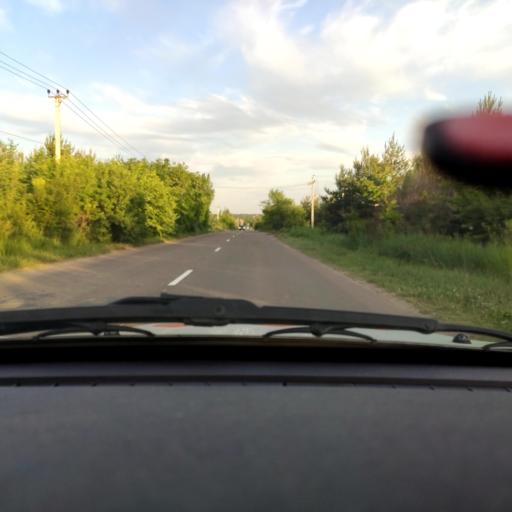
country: RU
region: Voronezj
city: Podgornoye
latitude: 51.8342
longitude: 39.2031
